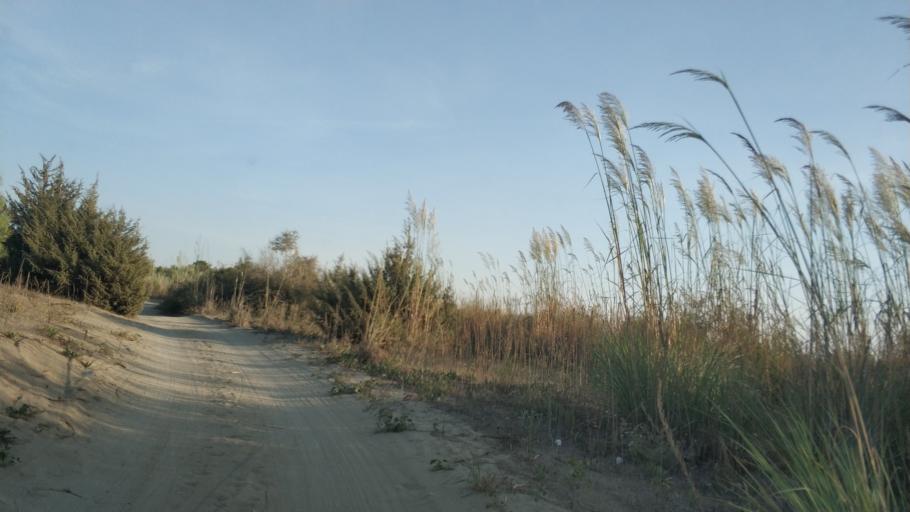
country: AL
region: Fier
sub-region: Rrethi i Lushnjes
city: Divjake
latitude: 40.9550
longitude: 19.4712
